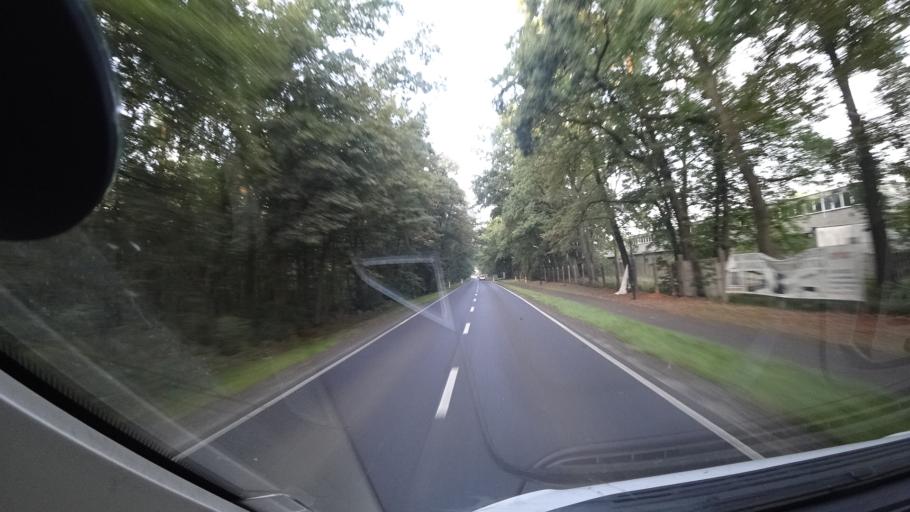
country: PL
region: Opole Voivodeship
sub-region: Powiat kedzierzynsko-kozielski
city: Slawiecice
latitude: 50.3662
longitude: 18.3006
